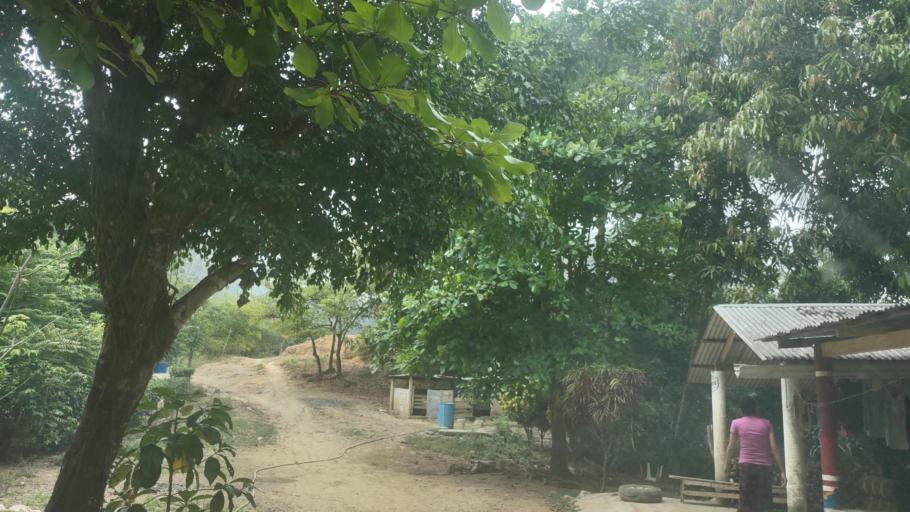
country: MX
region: Tabasco
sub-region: Huimanguillo
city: Francisco Rueda
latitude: 17.4456
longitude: -94.0251
